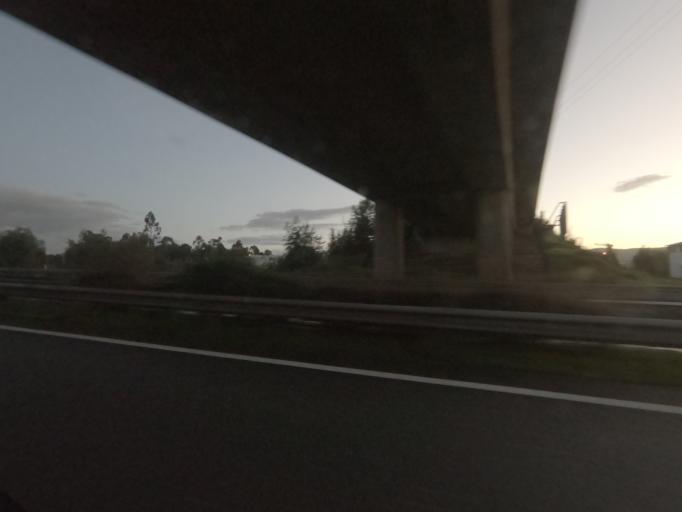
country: PT
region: Porto
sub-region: Paredes
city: Gandra
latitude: 41.1743
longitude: -8.4371
